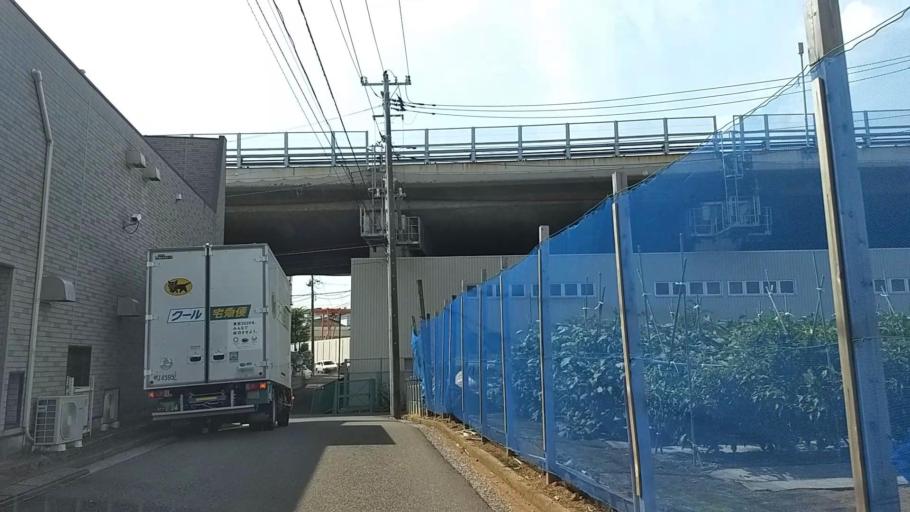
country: JP
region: Kanagawa
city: Yokohama
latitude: 35.5231
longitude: 139.5946
